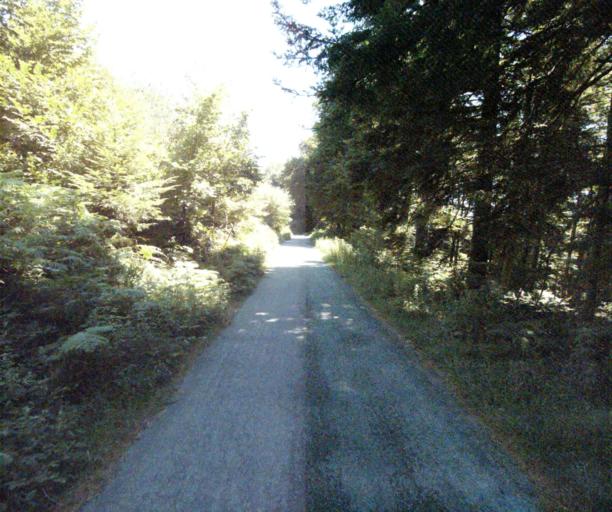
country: FR
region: Midi-Pyrenees
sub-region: Departement du Tarn
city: Dourgne
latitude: 43.4098
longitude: 2.1933
